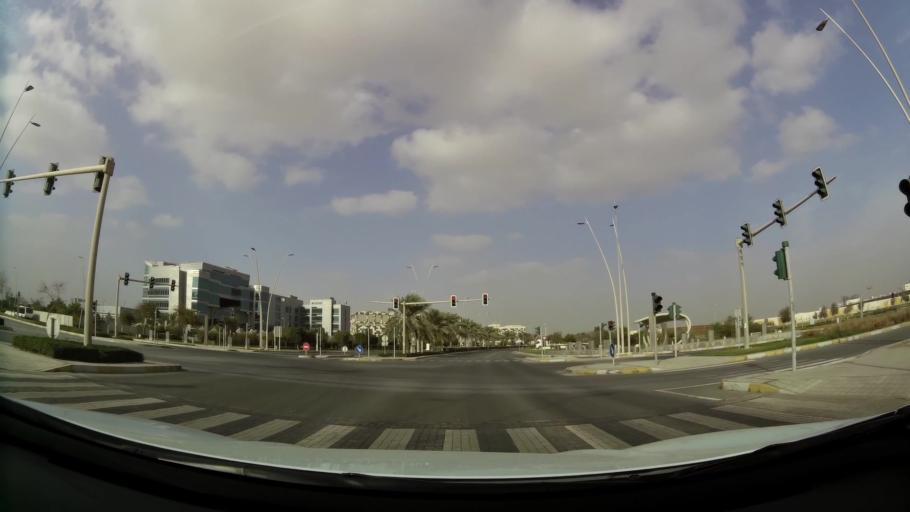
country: AE
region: Abu Dhabi
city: Abu Dhabi
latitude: 24.4916
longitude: 54.6033
